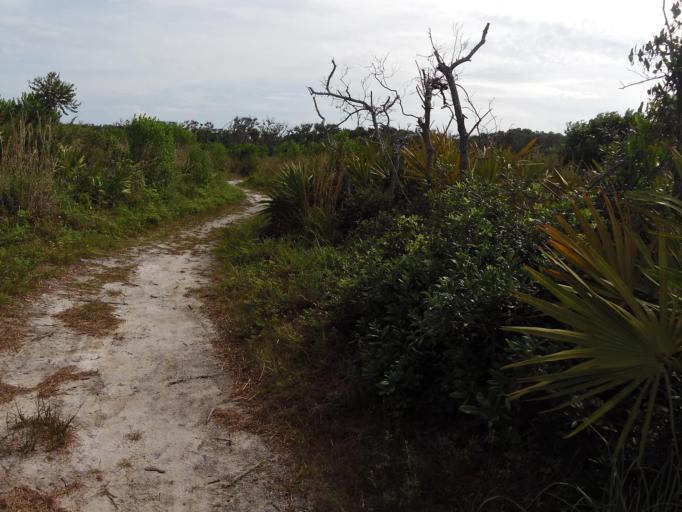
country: US
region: Florida
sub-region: Flagler County
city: Palm Coast
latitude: 29.6398
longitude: -81.2069
